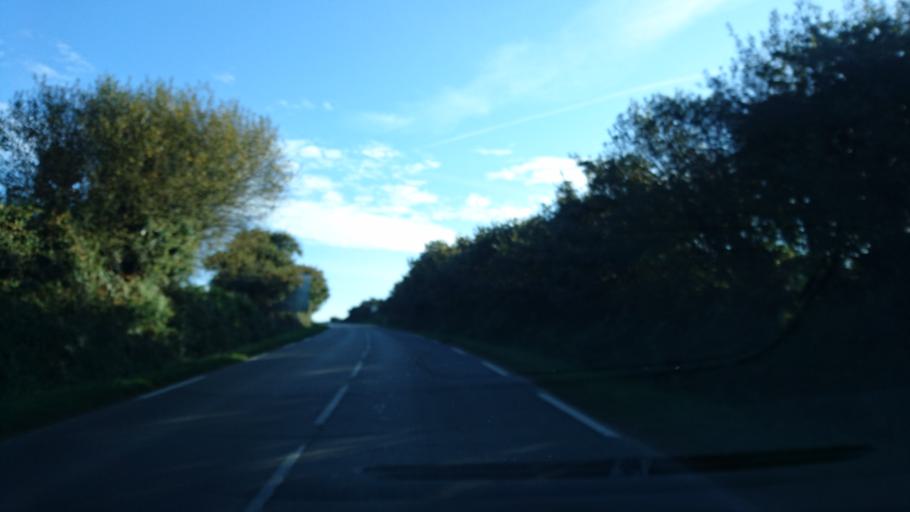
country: FR
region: Brittany
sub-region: Departement du Finistere
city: Saint-Renan
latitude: 48.4290
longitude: -4.5958
